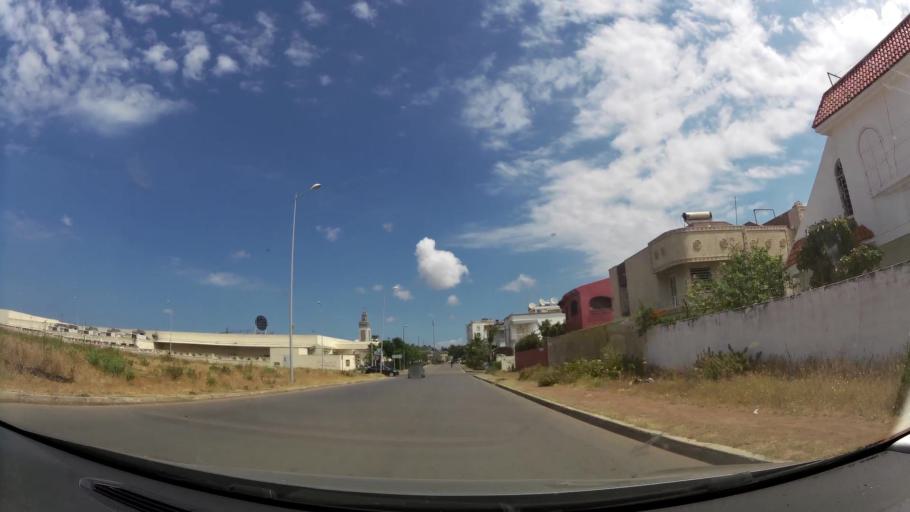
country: MA
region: Gharb-Chrarda-Beni Hssen
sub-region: Kenitra Province
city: Kenitra
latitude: 34.2462
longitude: -6.6077
